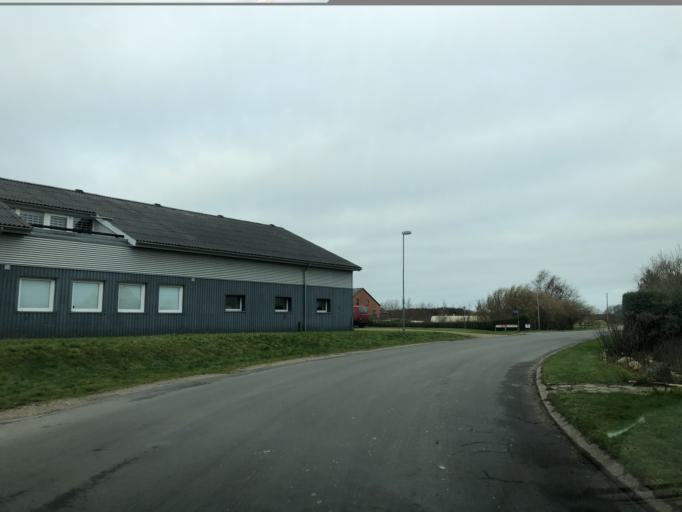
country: DK
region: Central Jutland
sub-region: Viborg Kommune
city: Stoholm
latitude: 56.4868
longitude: 9.1558
